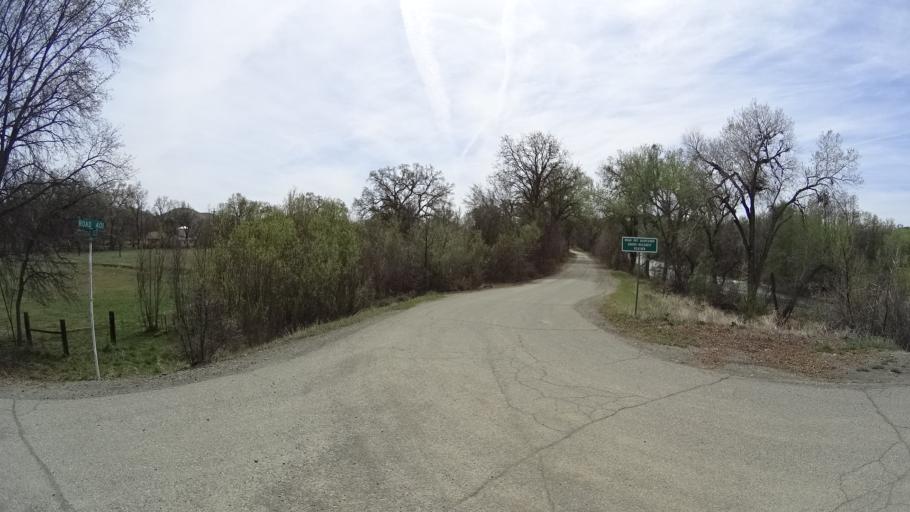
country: US
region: California
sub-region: Glenn County
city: Willows
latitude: 39.4347
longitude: -122.5027
